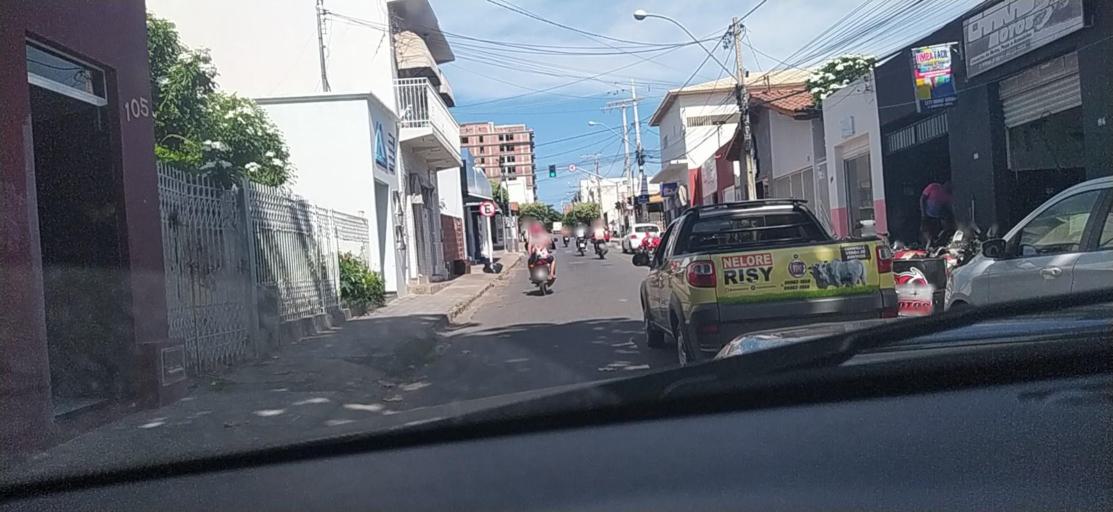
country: BR
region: Bahia
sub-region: Guanambi
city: Guanambi
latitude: -14.2216
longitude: -42.7810
